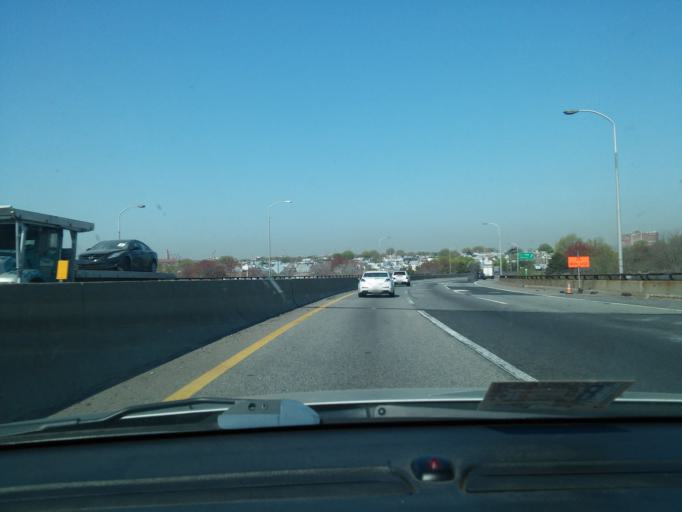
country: US
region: New Jersey
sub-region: Hudson County
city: Bayonne
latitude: 40.6859
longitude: -74.0944
